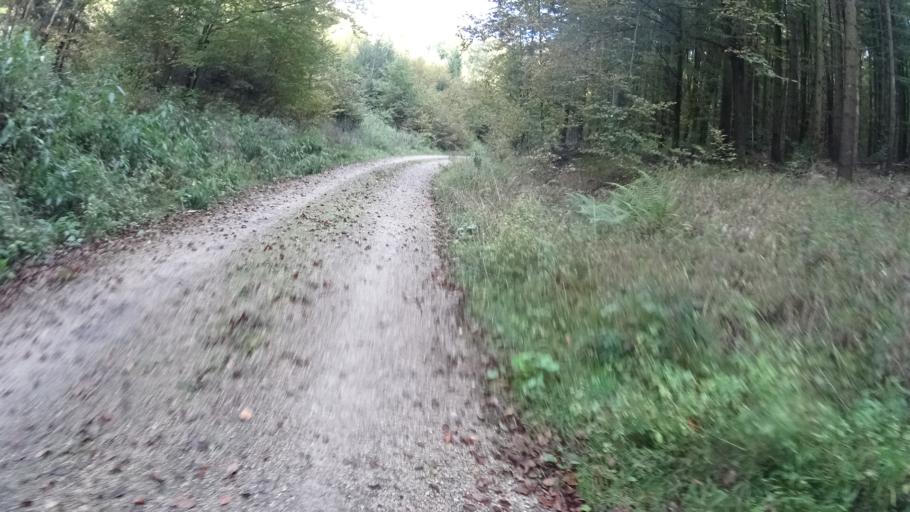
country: DE
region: Bavaria
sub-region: Upper Bavaria
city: Walting
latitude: 48.9023
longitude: 11.3158
